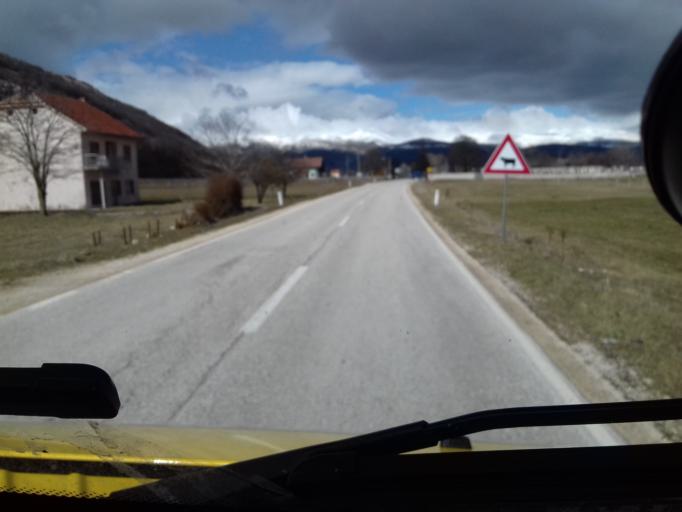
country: BA
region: Federation of Bosnia and Herzegovina
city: Tomislavgrad
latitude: 43.6610
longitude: 17.2100
